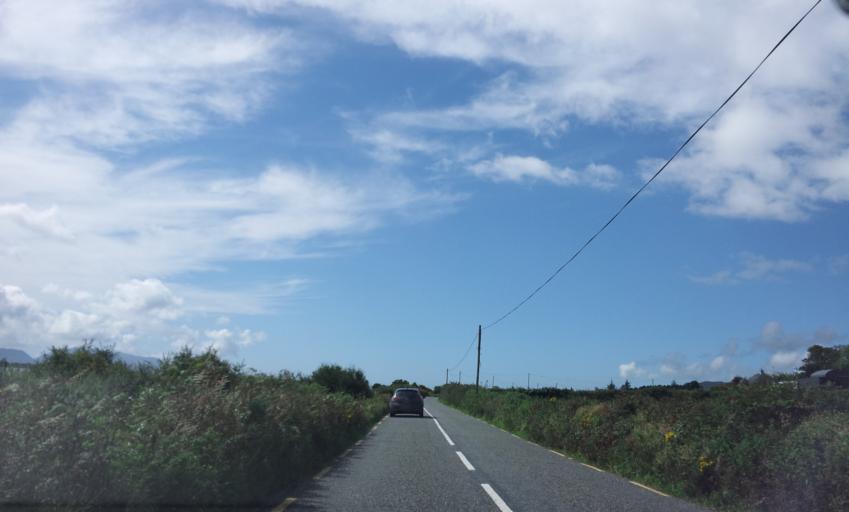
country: IE
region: Munster
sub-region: Ciarrai
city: Killorglin
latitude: 52.1500
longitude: -9.9200
